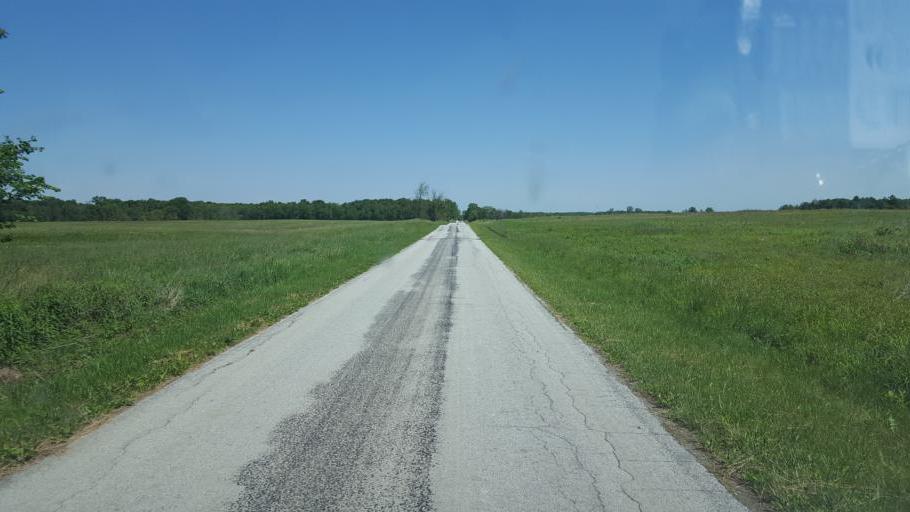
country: US
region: Ohio
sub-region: Hardin County
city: Kenton
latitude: 40.6300
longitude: -83.4387
